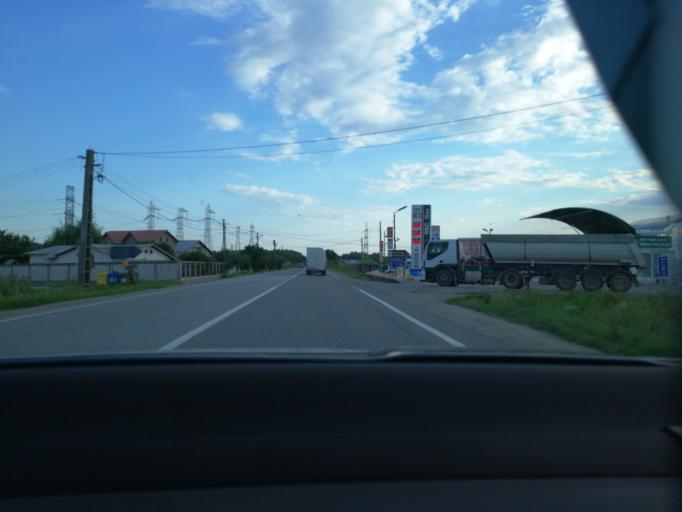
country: RO
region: Prahova
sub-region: Comuna Targsoru Vechi
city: Targsoru Vechi
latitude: 44.8624
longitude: 25.9279
